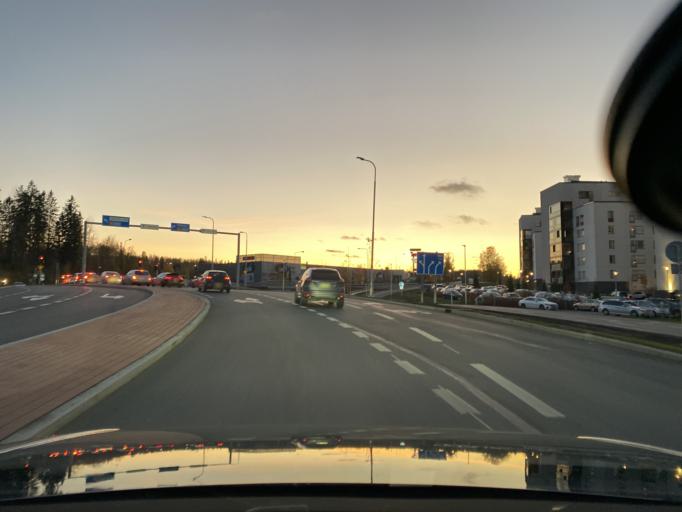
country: FI
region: Pirkanmaa
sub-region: Tampere
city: Tampere
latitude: 61.4706
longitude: 23.7220
